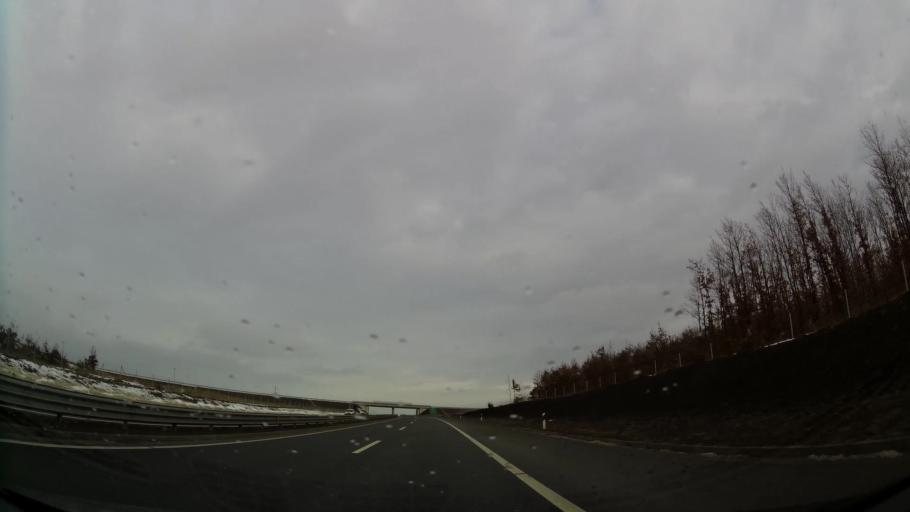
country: XK
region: Ferizaj
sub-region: Komuna e Ferizajt
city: Ferizaj
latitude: 42.3476
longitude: 21.2056
